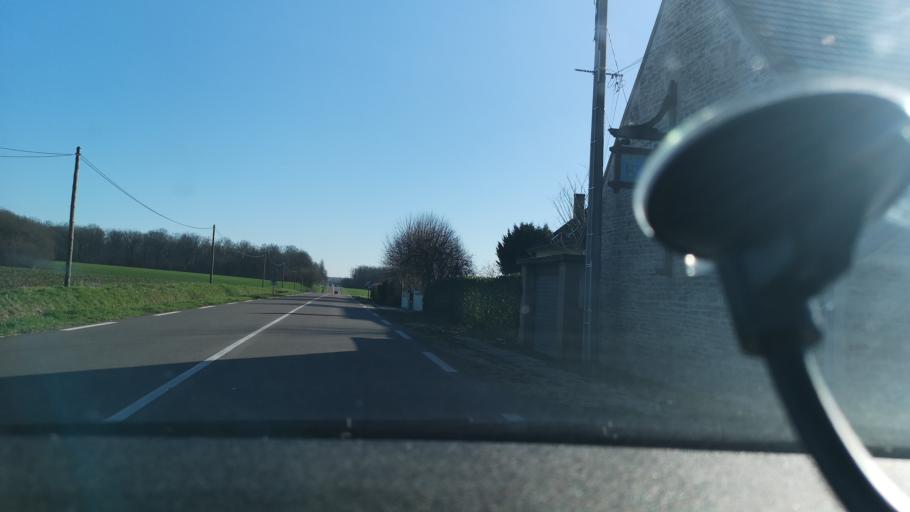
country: FR
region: Bourgogne
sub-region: Departement de Saone-et-Loire
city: Ouroux-sur-Saone
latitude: 46.7693
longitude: 4.9790
